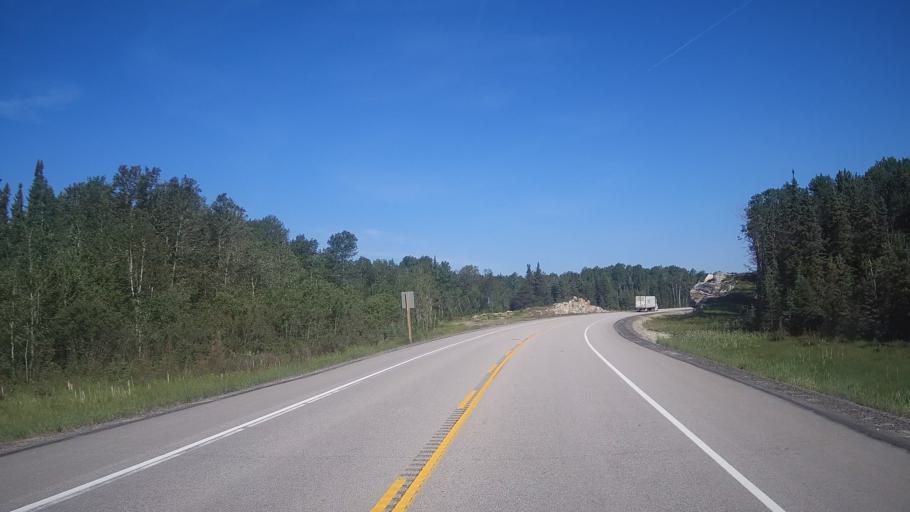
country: CA
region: Ontario
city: Dryden
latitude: 49.5730
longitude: -92.2575
